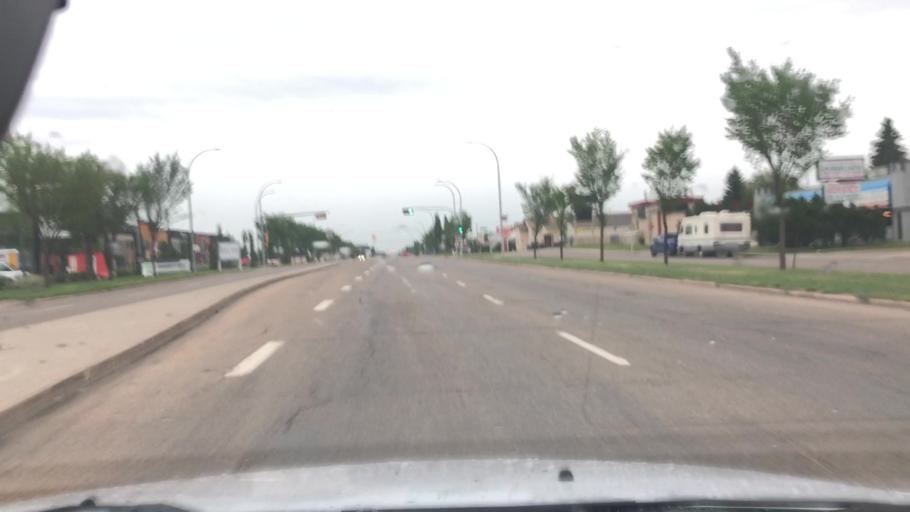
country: CA
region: Alberta
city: St. Albert
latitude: 53.5589
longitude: -113.5886
